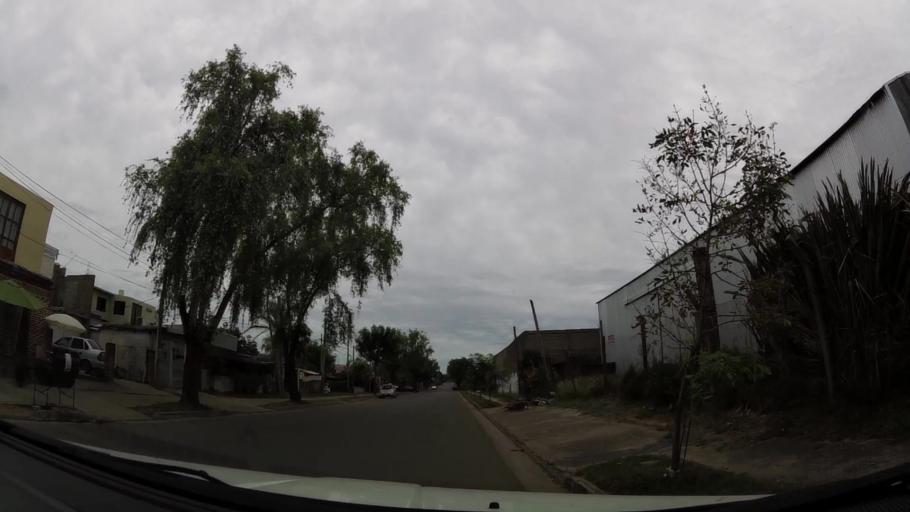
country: UY
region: Maldonado
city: Maldonado
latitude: -34.8895
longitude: -54.9399
